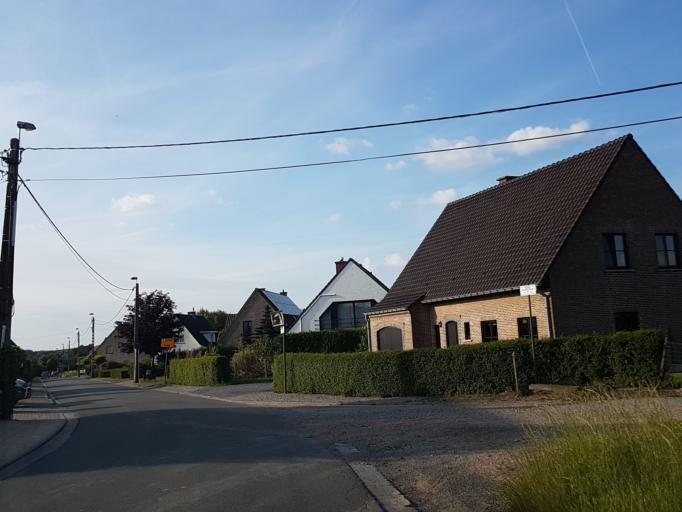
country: BE
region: Flanders
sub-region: Provincie Oost-Vlaanderen
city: Denderleeuw
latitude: 50.9357
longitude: 4.1012
